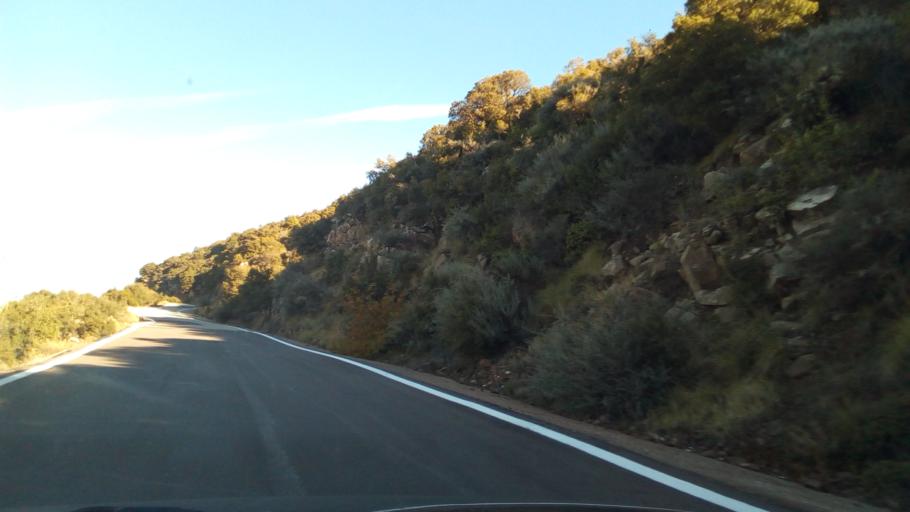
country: GR
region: West Greece
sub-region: Nomos Aitolias kai Akarnanias
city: Nafpaktos
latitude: 38.5061
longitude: 21.8374
